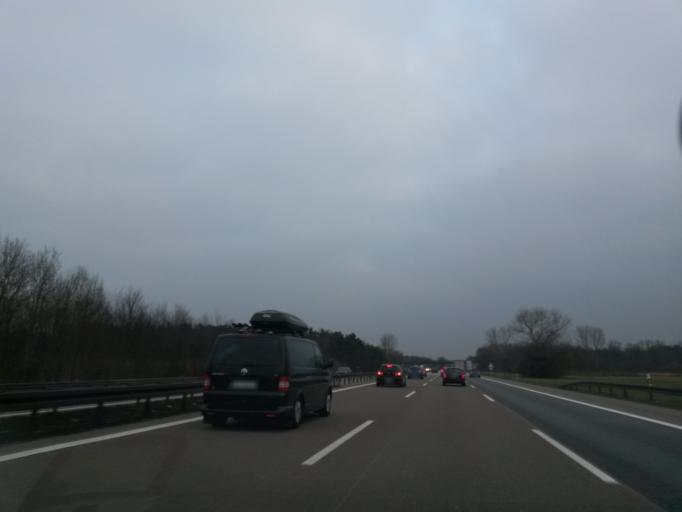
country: DE
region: Bavaria
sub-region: Upper Bavaria
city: Manching
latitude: 48.6869
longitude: 11.4968
